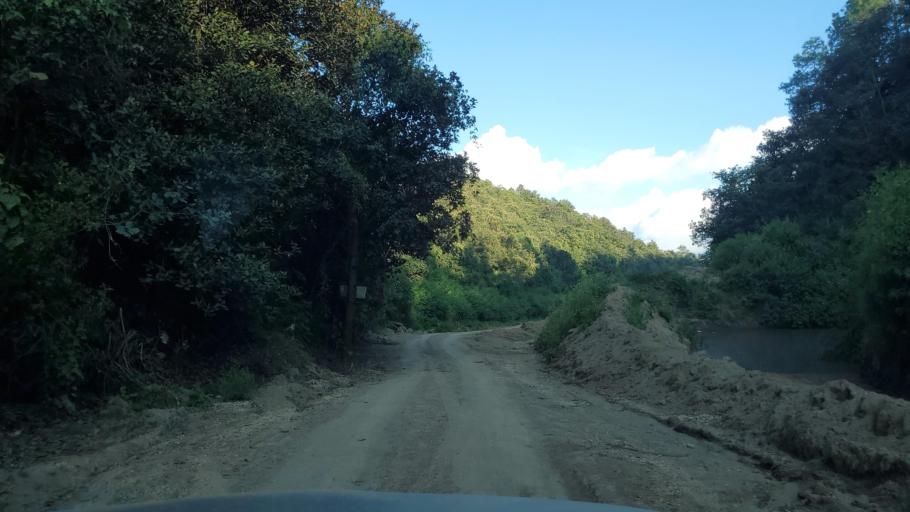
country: GT
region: Quetzaltenango
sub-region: Municipio de La Esperanza
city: La Esperanza
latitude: 14.8395
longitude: -91.5550
